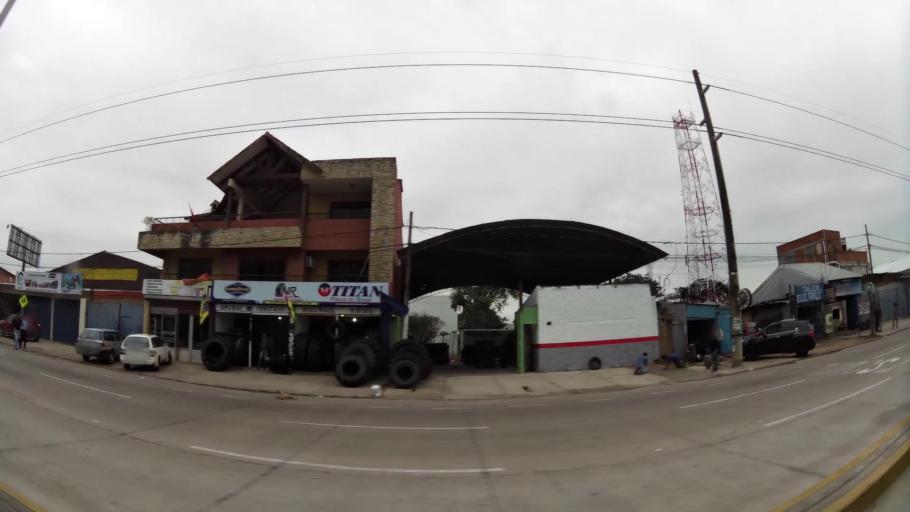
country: BO
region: Santa Cruz
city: Santa Cruz de la Sierra
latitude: -17.7891
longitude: -63.2049
